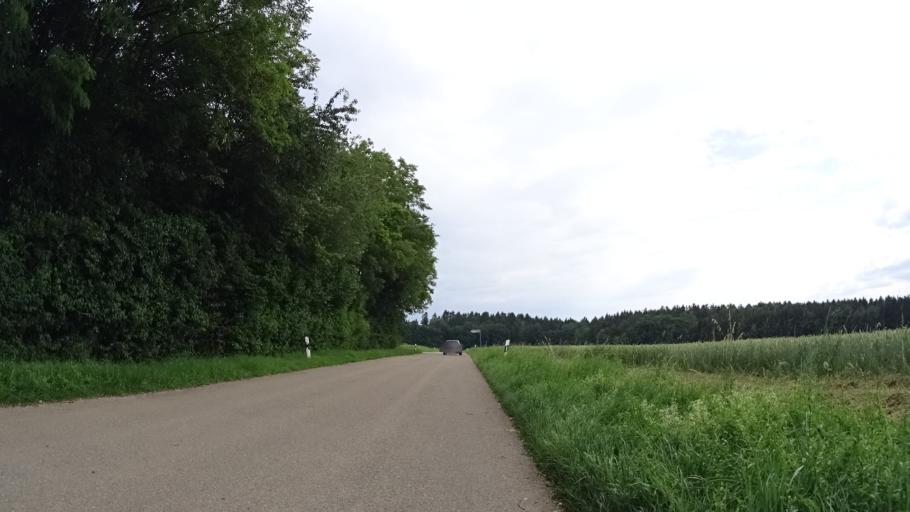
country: DE
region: Bavaria
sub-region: Upper Bavaria
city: Wettstetten
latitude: 48.8334
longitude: 11.4291
